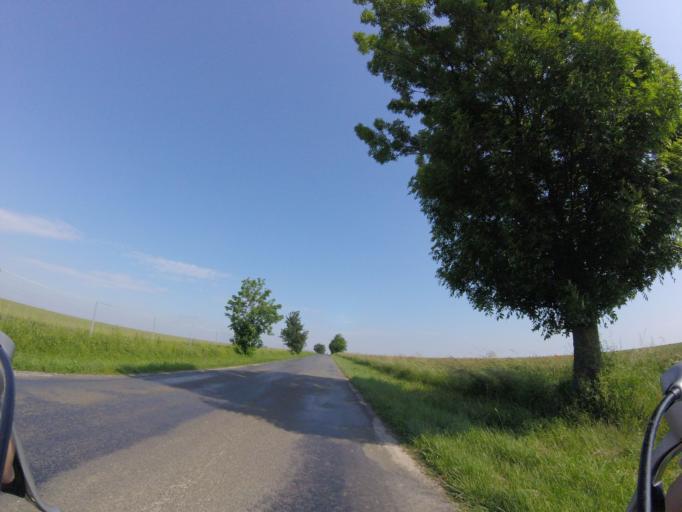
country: HU
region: Baranya
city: Villany
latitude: 45.9230
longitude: 18.3712
